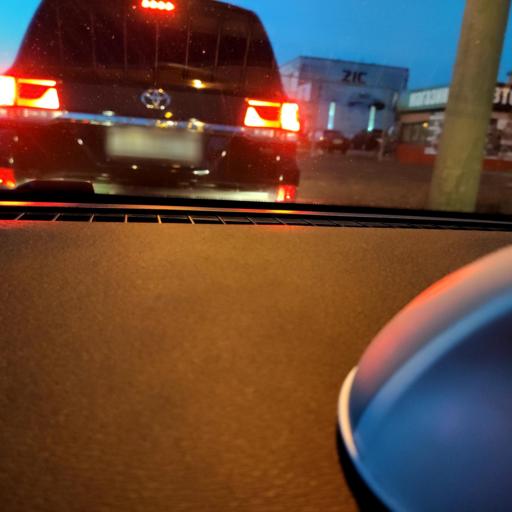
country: RU
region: Samara
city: Petra-Dubrava
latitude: 53.2544
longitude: 50.2664
